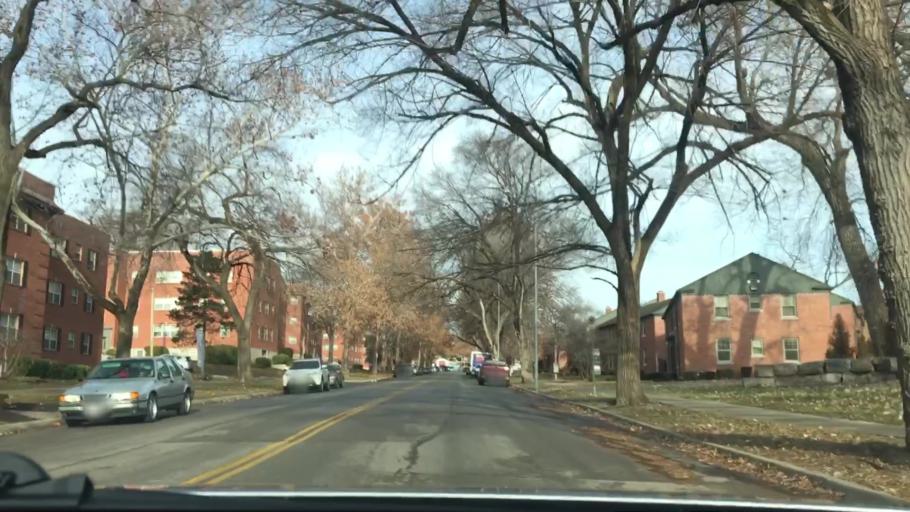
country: US
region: Kansas
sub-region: Johnson County
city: Westwood
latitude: 39.0465
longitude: -94.6008
